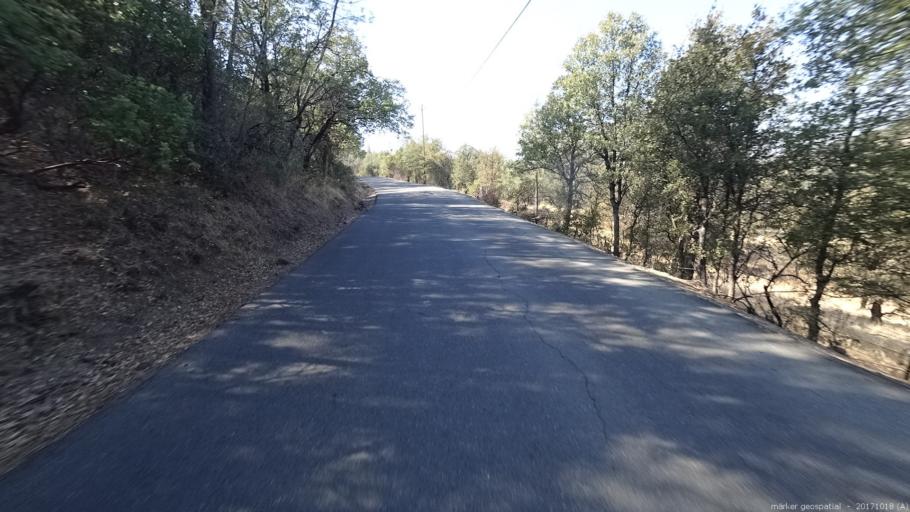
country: US
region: California
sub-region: Shasta County
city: Palo Cedro
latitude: 40.5451
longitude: -122.1003
